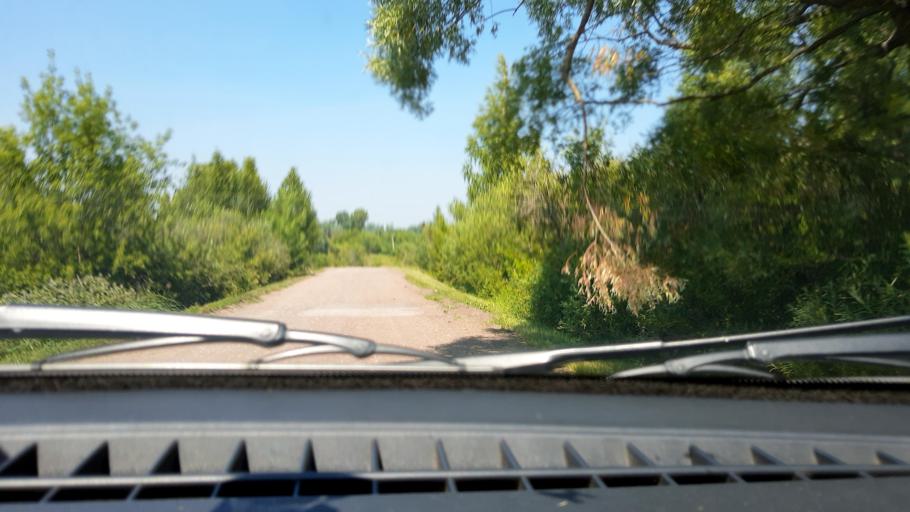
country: RU
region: Bashkortostan
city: Kushnarenkovo
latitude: 55.0659
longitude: 55.1640
